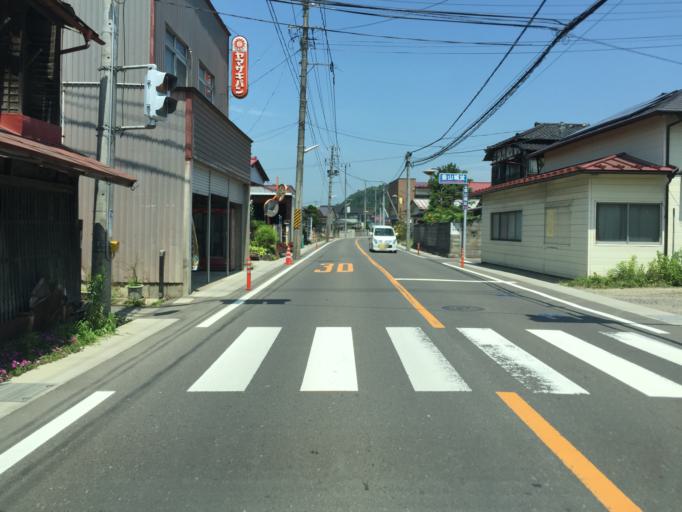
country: JP
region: Miyagi
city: Marumori
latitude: 37.9001
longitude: 140.7994
